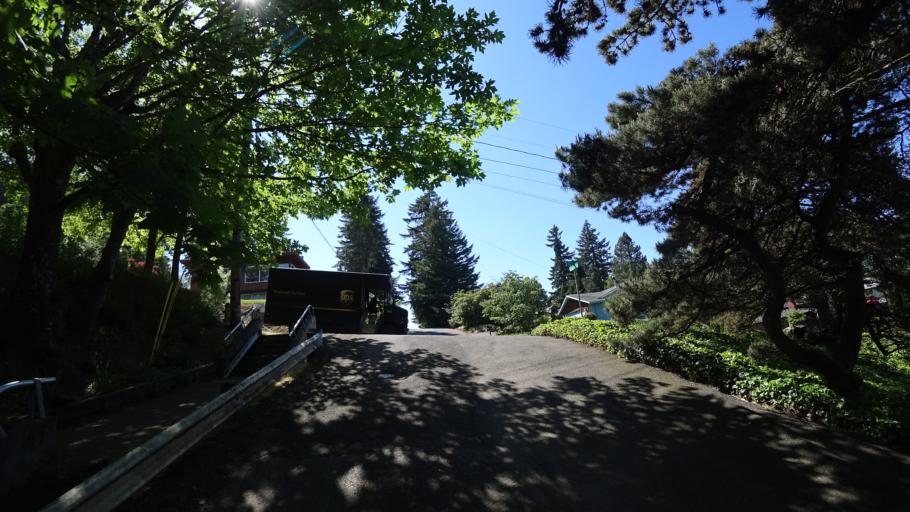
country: US
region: Oregon
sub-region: Washington County
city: Metzger
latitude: 45.4492
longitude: -122.7189
